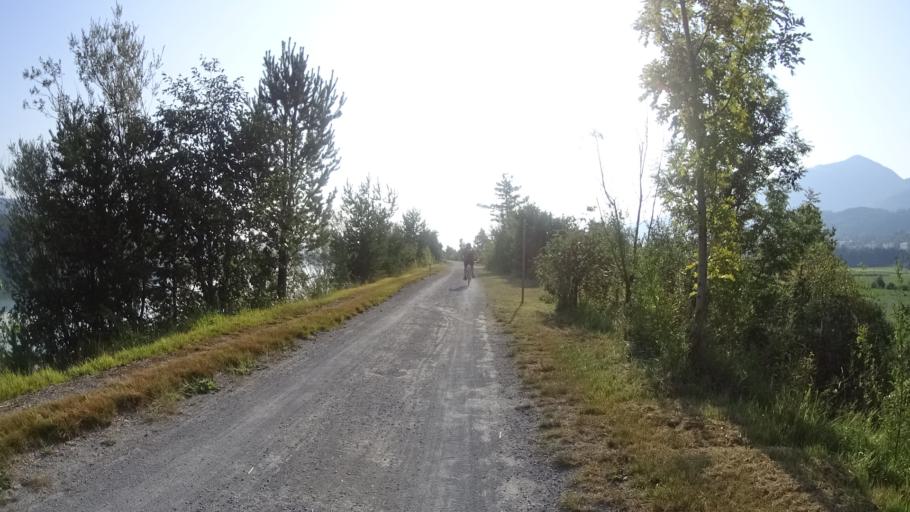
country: AT
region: Carinthia
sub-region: Politischer Bezirk Klagenfurt Land
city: Feistritz im Rosental
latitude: 46.5291
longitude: 14.1554
